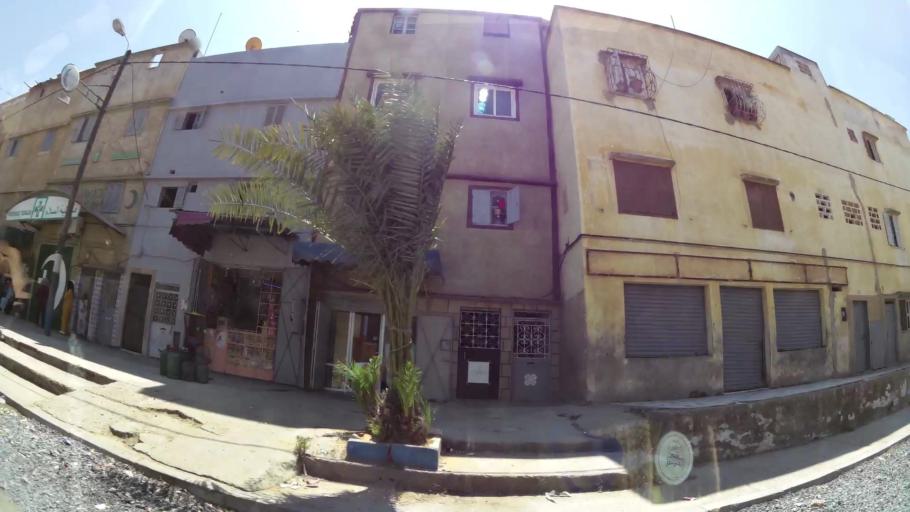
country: MA
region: Gharb-Chrarda-Beni Hssen
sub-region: Kenitra Province
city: Kenitra
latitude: 34.2519
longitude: -6.5416
